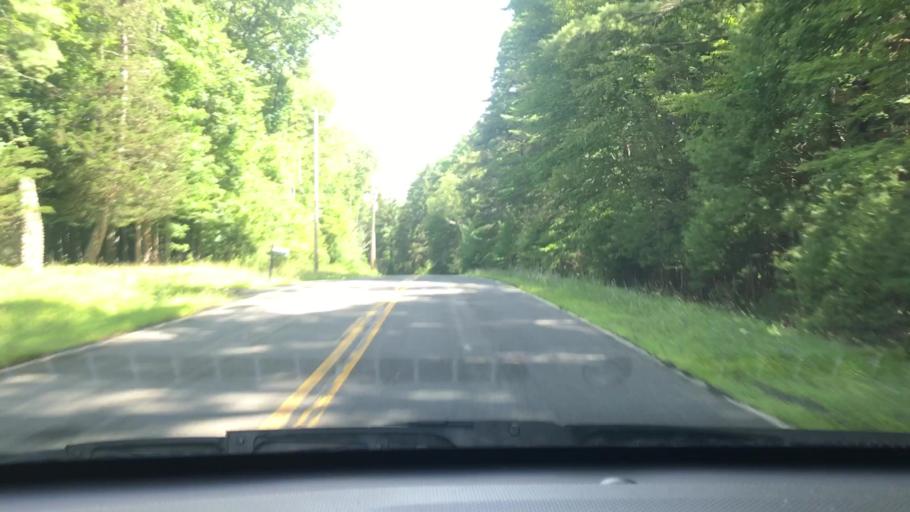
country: US
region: New York
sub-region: Ulster County
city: Shokan
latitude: 41.9352
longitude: -74.2444
